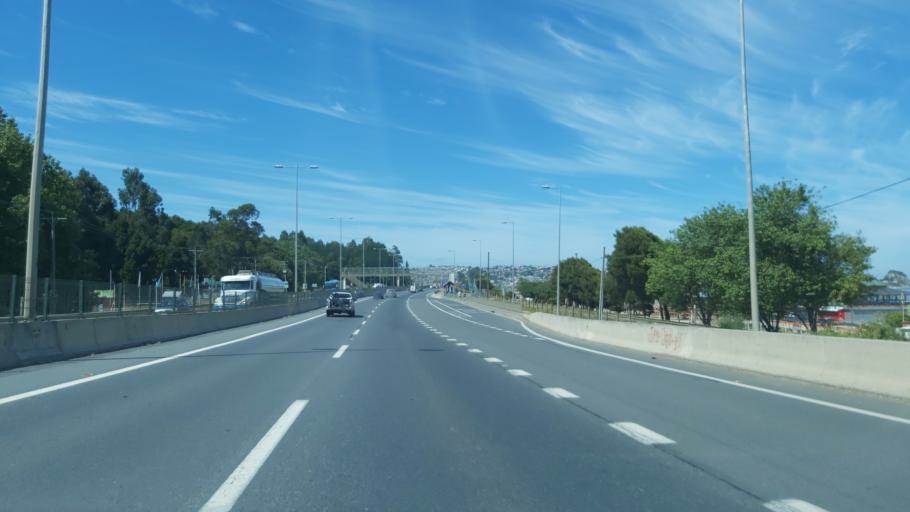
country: CL
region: Biobio
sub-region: Provincia de Concepcion
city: Coronel
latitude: -37.0613
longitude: -73.1408
